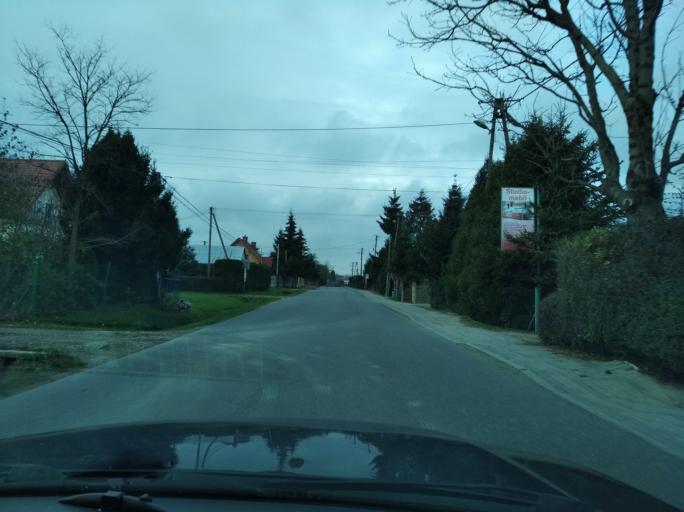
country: PL
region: Subcarpathian Voivodeship
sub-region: Powiat krosnienski
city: Kroscienko Wyzne
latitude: 49.6776
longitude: 21.8143
